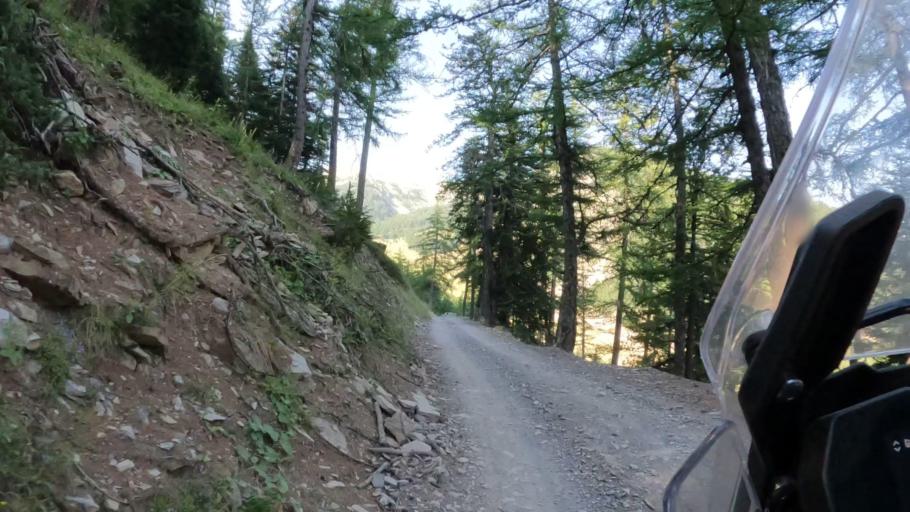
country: FR
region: Provence-Alpes-Cote d'Azur
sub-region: Departement des Hautes-Alpes
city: Guillestre
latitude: 44.5877
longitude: 6.6024
